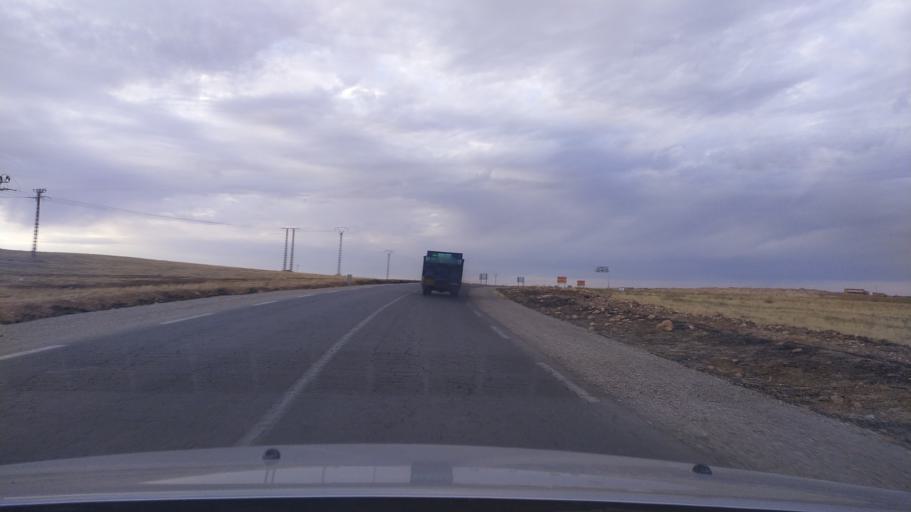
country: DZ
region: Tiaret
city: Frenda
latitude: 34.9883
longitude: 1.1321
